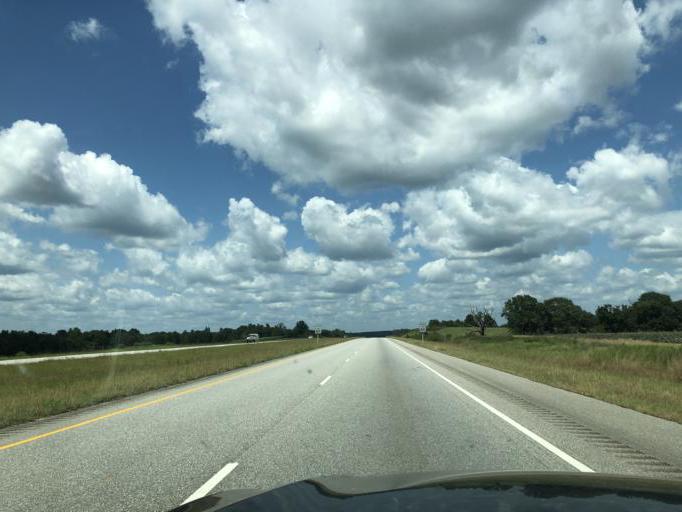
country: US
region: Alabama
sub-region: Barbour County
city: Eufaula
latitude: 32.0927
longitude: -85.1498
